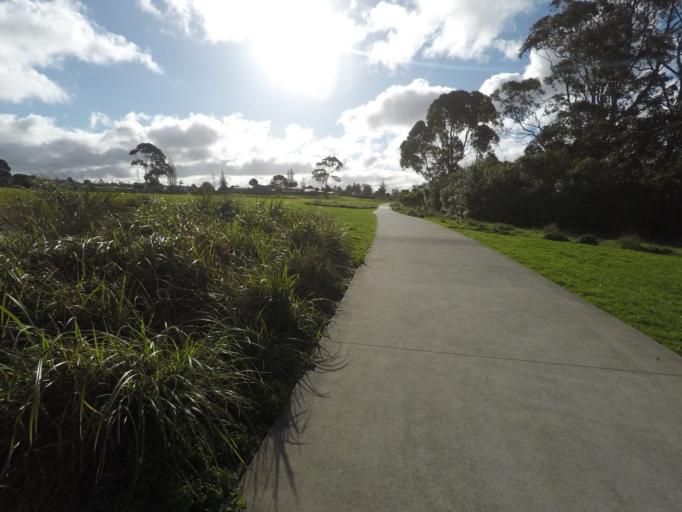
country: NZ
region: Auckland
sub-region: Auckland
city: Rosebank
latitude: -36.8931
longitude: 174.6716
